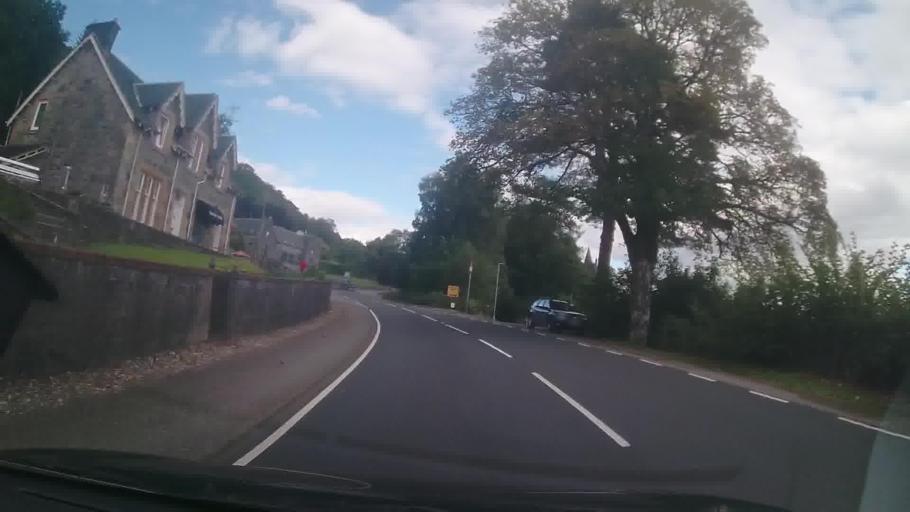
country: GB
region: Scotland
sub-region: Argyll and Bute
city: Garelochhead
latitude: 56.4011
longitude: -5.0459
